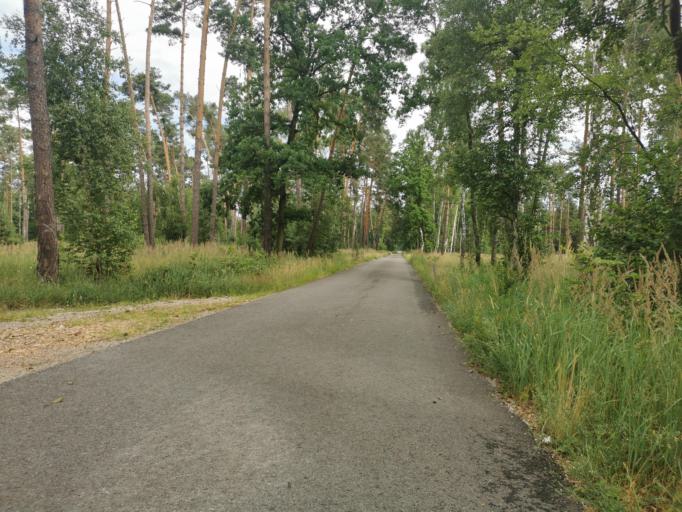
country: SK
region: Trnavsky
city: Gbely
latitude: 48.7405
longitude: 17.0858
